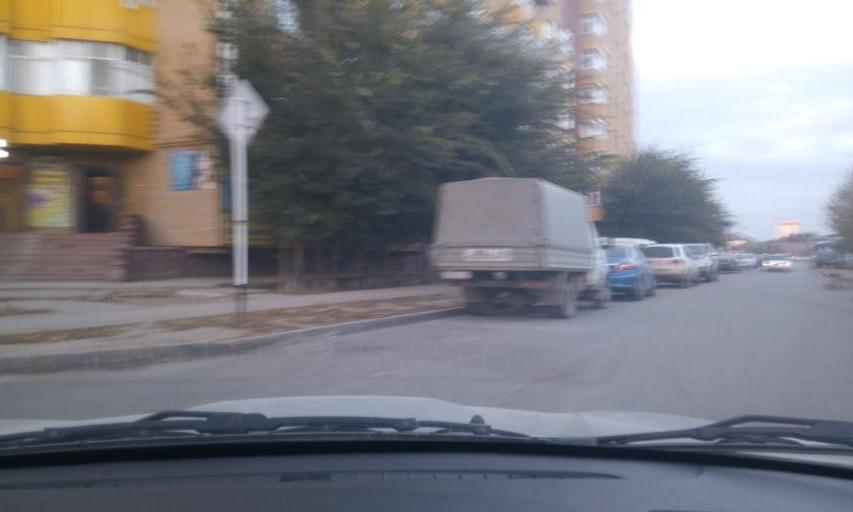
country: KZ
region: Astana Qalasy
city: Astana
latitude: 51.1404
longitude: 71.4856
